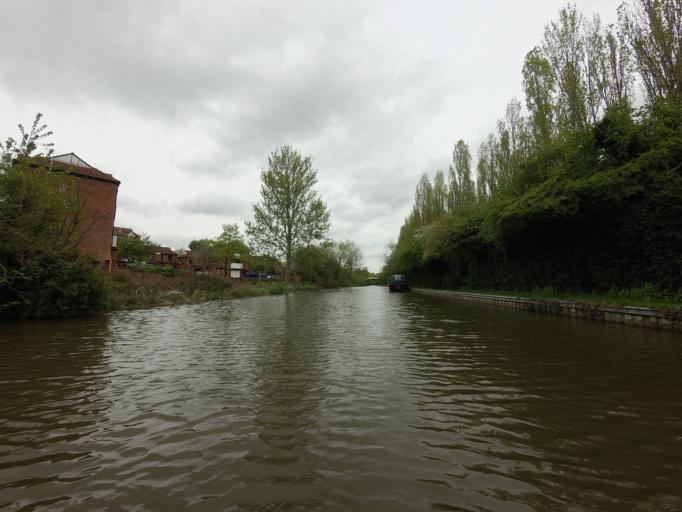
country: GB
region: England
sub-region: Milton Keynes
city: Milton Keynes
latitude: 52.0380
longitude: -0.7324
